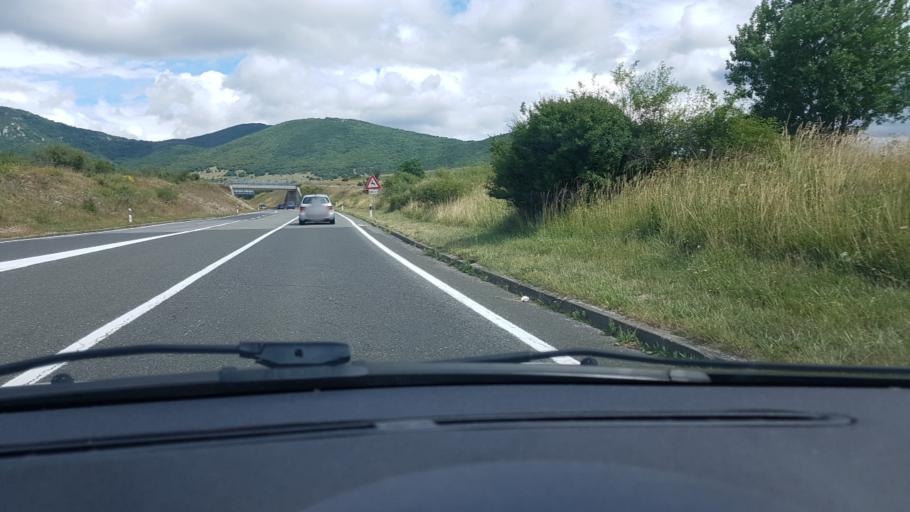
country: HR
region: Zadarska
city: Gracac
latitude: 44.5070
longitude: 15.7490
